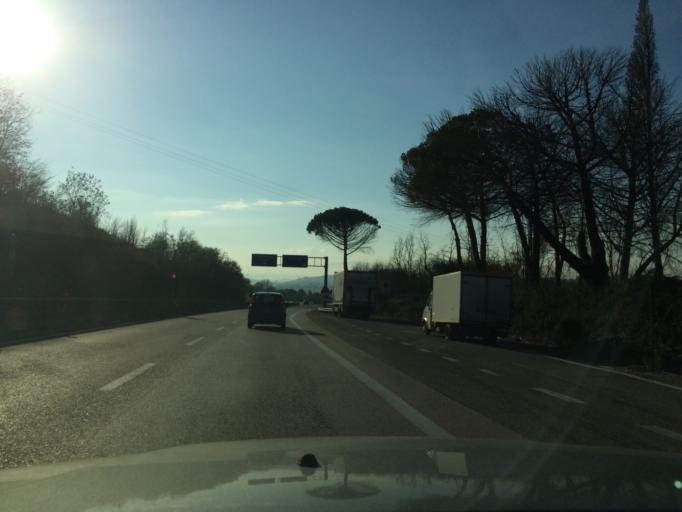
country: IT
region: Umbria
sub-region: Provincia di Terni
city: Fornole
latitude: 42.5324
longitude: 12.4773
